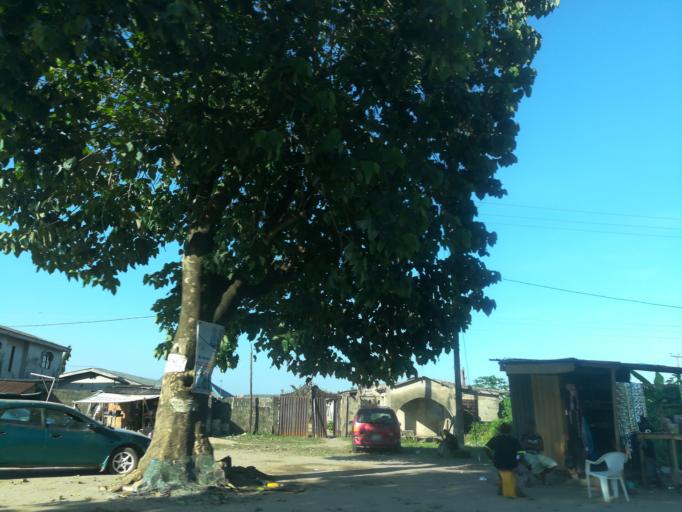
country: NG
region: Lagos
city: Ebute Ikorodu
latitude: 6.5444
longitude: 3.5445
